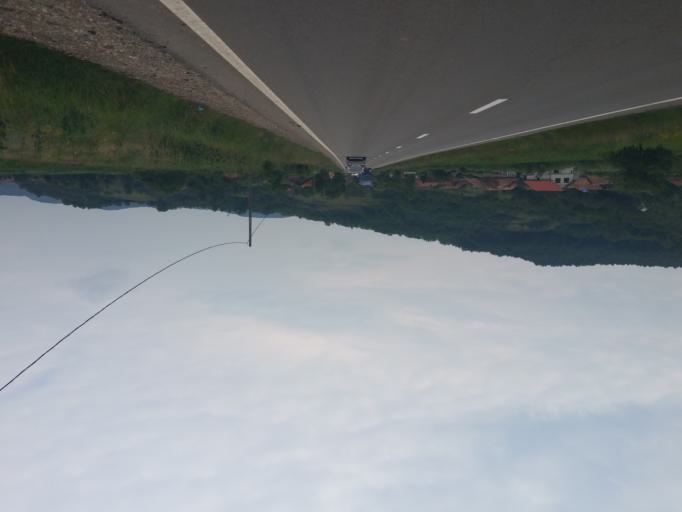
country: RO
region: Salaj
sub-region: Comuna Zimbor
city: Zimbor
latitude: 47.0219
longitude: 23.2636
